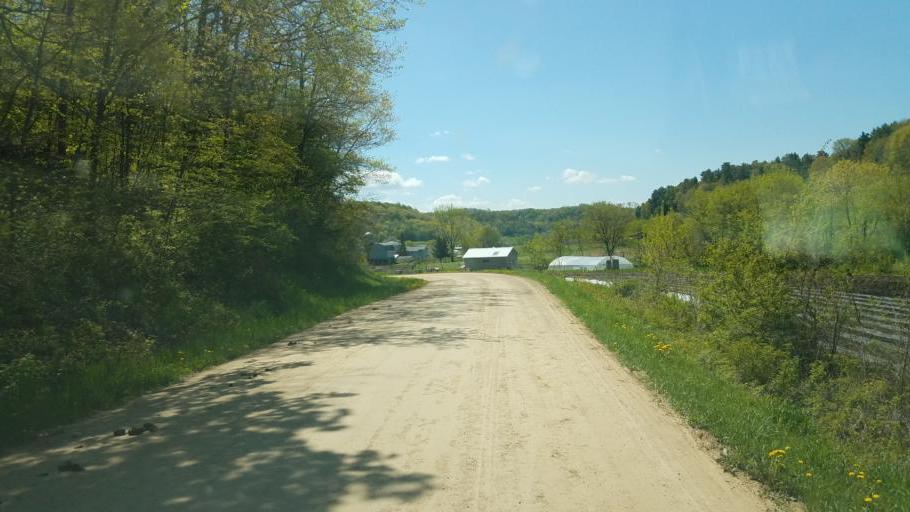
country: US
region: Wisconsin
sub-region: Vernon County
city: Hillsboro
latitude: 43.5912
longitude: -90.4091
